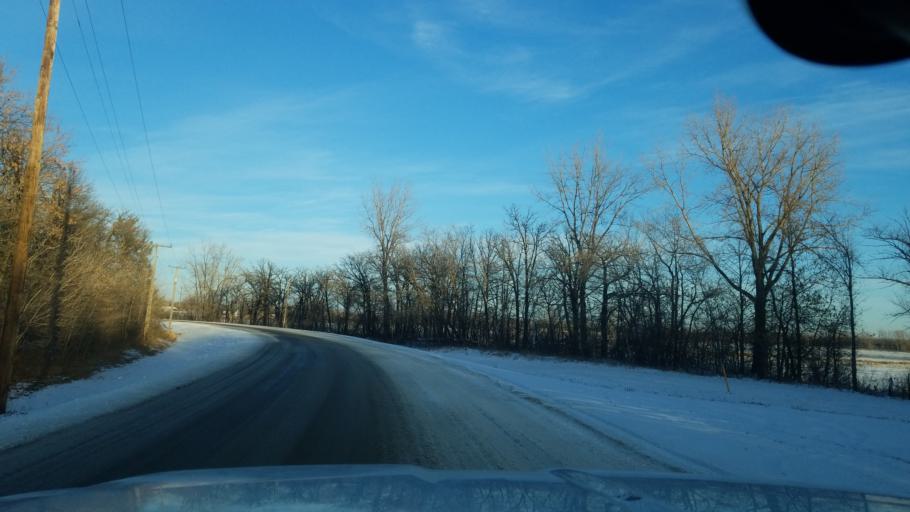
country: CA
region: Manitoba
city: Portage la Prairie
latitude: 49.9456
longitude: -98.3415
